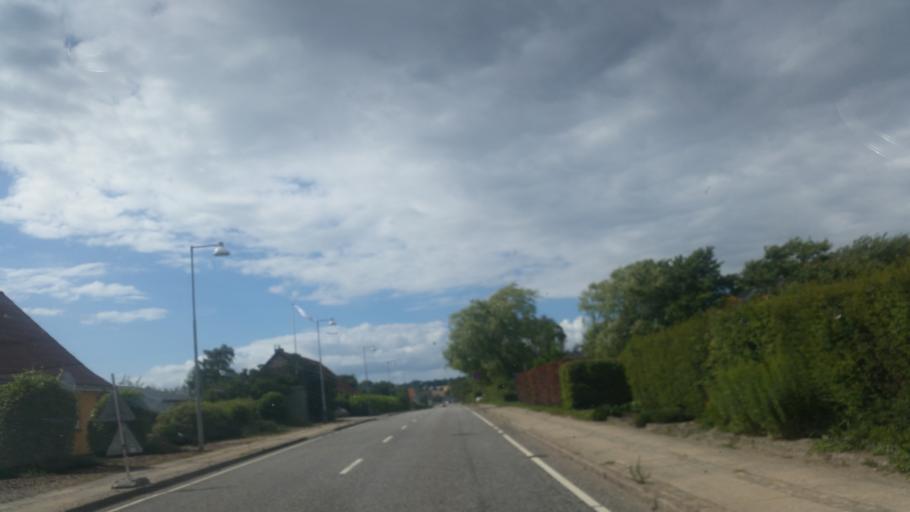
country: DK
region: Zealand
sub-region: Odsherred Kommune
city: Horve
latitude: 55.7999
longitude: 11.4456
